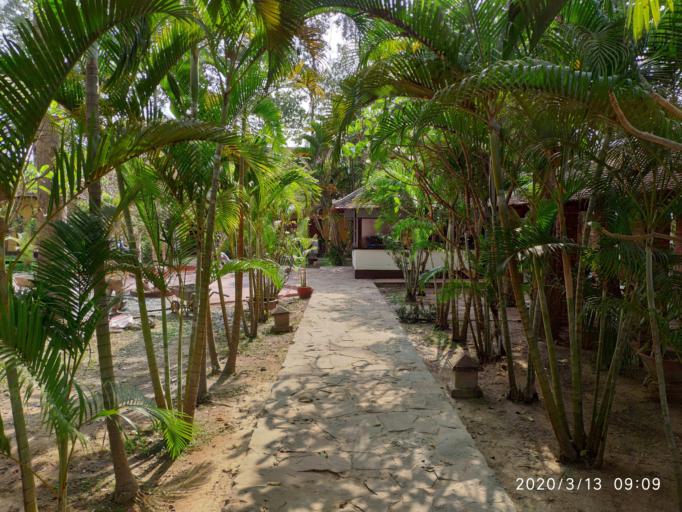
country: KH
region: Siem Reap
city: Siem Reap
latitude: 13.4367
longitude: 103.7450
